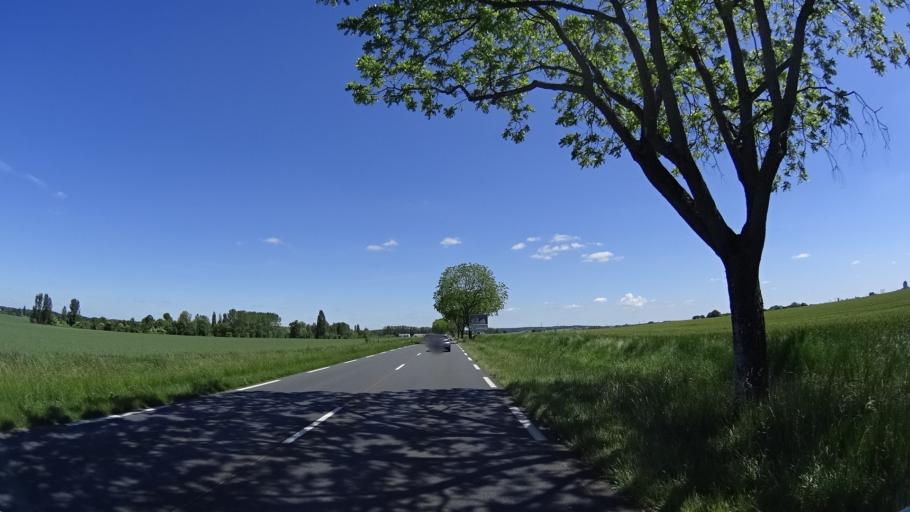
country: FR
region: Pays de la Loire
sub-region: Departement de Maine-et-Loire
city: Distre
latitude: 47.2203
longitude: -0.1566
